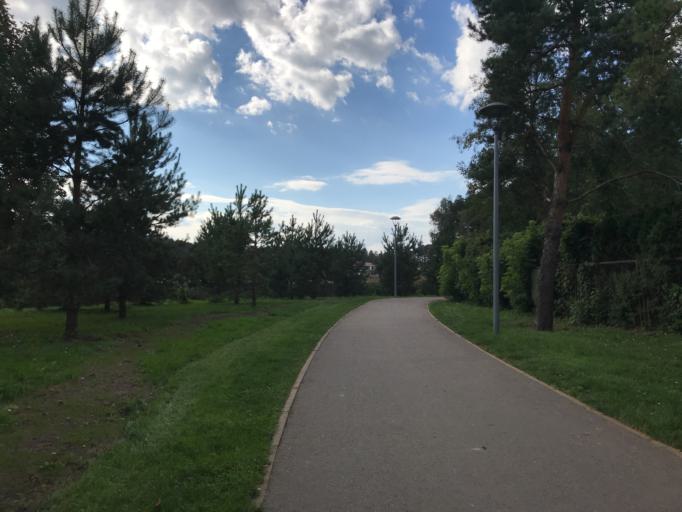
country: LT
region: Alytaus apskritis
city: Druskininkai
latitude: 54.0171
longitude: 23.9652
